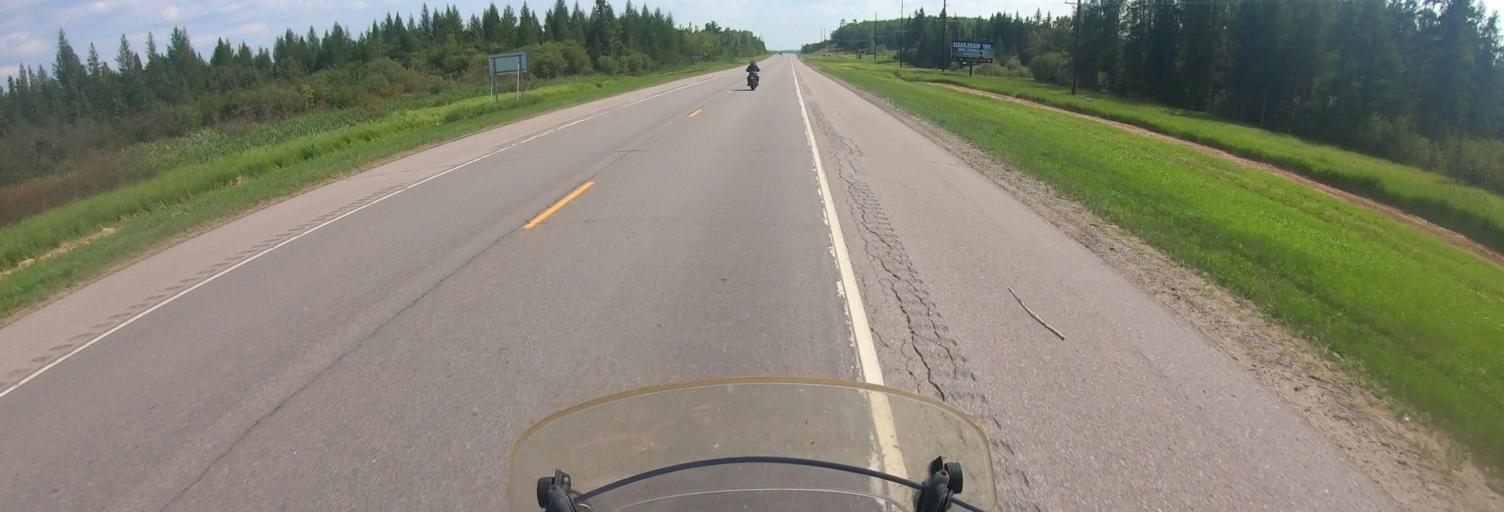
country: US
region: Minnesota
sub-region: Saint Louis County
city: Chisholm
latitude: 47.9619
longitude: -92.8294
